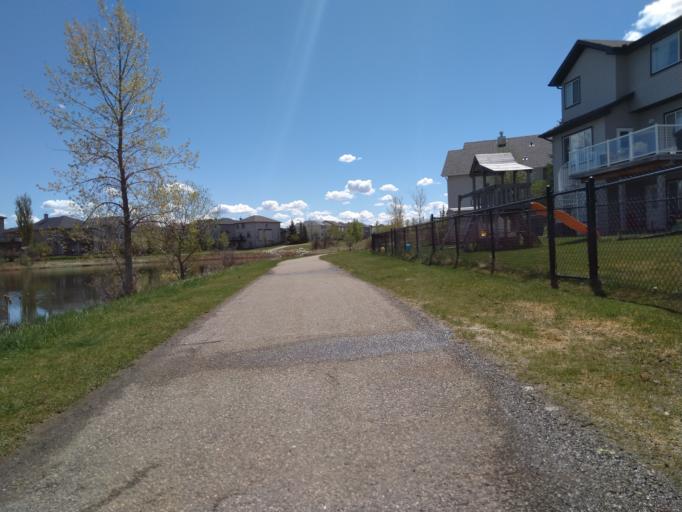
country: CA
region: Alberta
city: Chestermere
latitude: 51.0334
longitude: -113.8386
